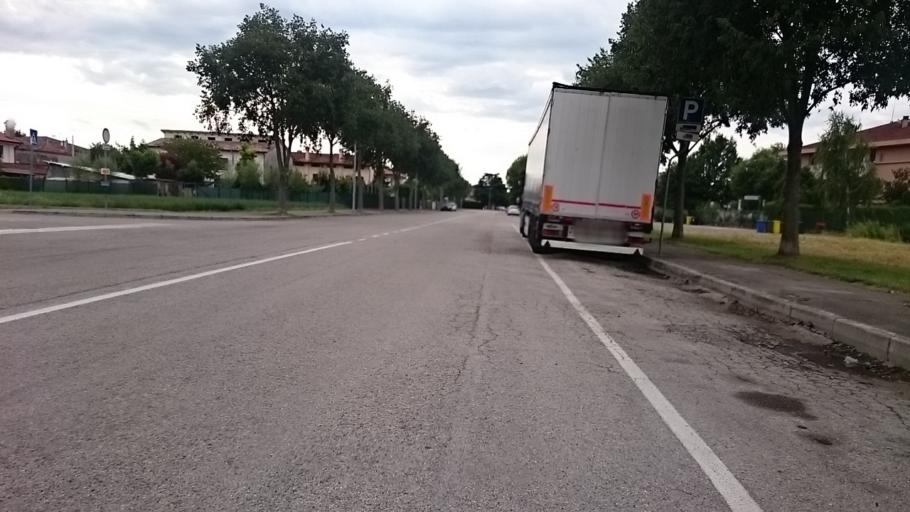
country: IT
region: Veneto
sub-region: Provincia di Padova
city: Albignasego
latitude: 45.3458
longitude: 11.8725
